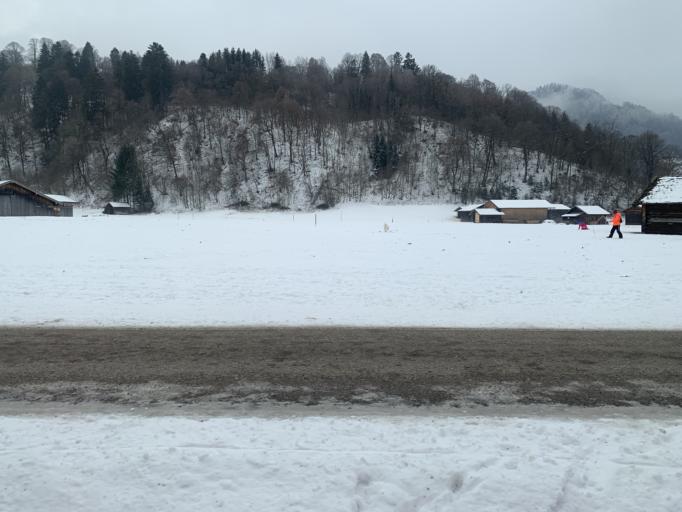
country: DE
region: Bavaria
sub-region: Upper Bavaria
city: Garmisch-Partenkirchen
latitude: 47.4848
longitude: 11.1056
